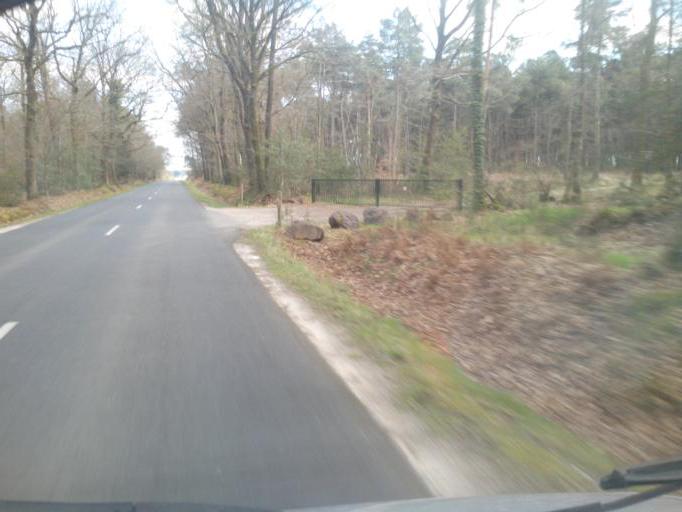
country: FR
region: Brittany
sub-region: Departement d'Ille-et-Vilaine
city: Plelan-le-Grand
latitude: 48.0113
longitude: -2.1316
